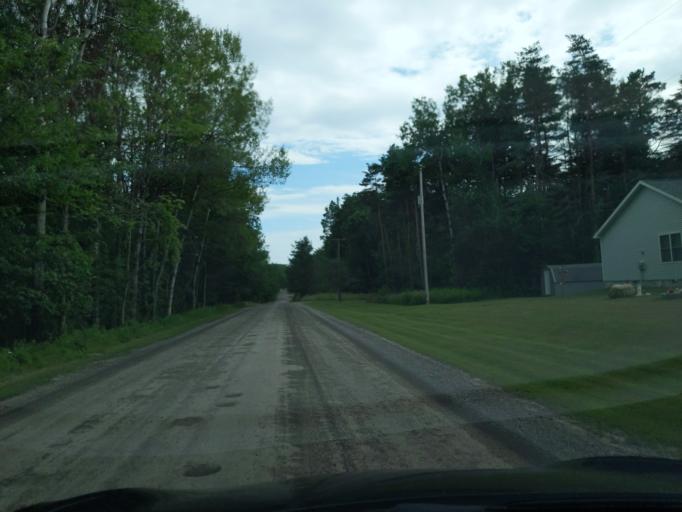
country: US
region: Michigan
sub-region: Clare County
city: Harrison
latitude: 43.9787
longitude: -84.9983
